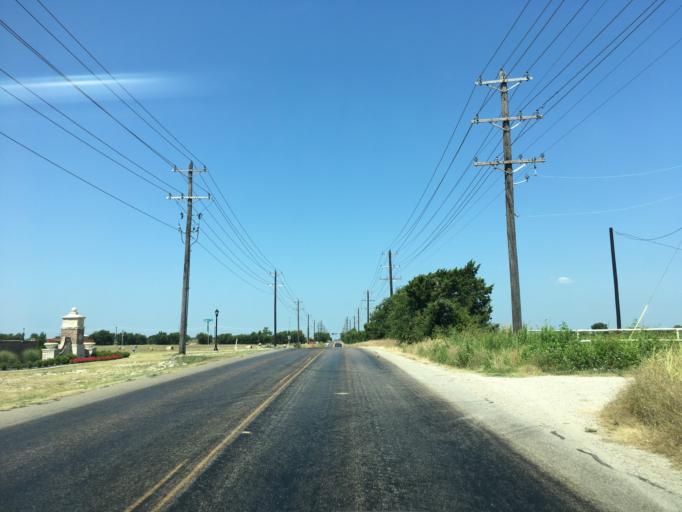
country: US
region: Texas
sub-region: Collin County
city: Prosper
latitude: 33.2039
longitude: -96.7812
